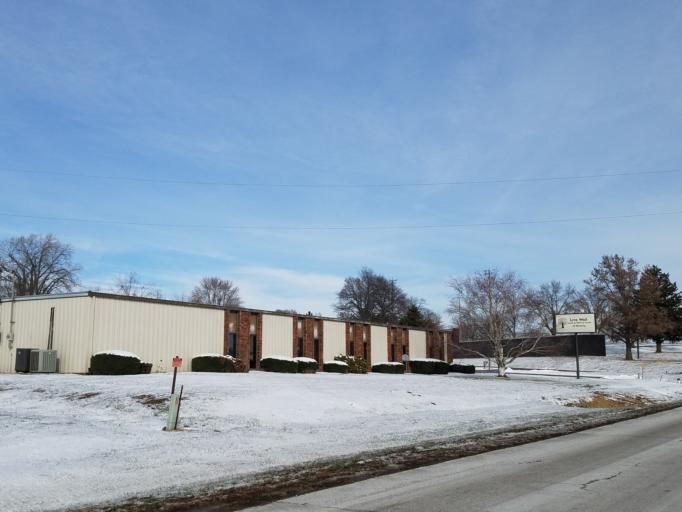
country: US
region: Missouri
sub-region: Carroll County
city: Carrollton
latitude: 39.2057
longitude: -93.5305
